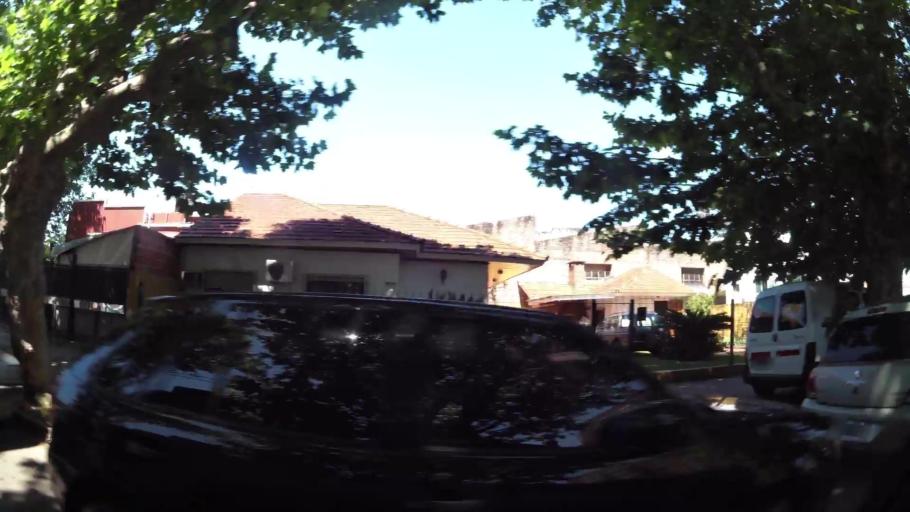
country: AR
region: Buenos Aires
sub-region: Partido de Tigre
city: Tigre
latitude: -34.4289
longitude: -58.5716
